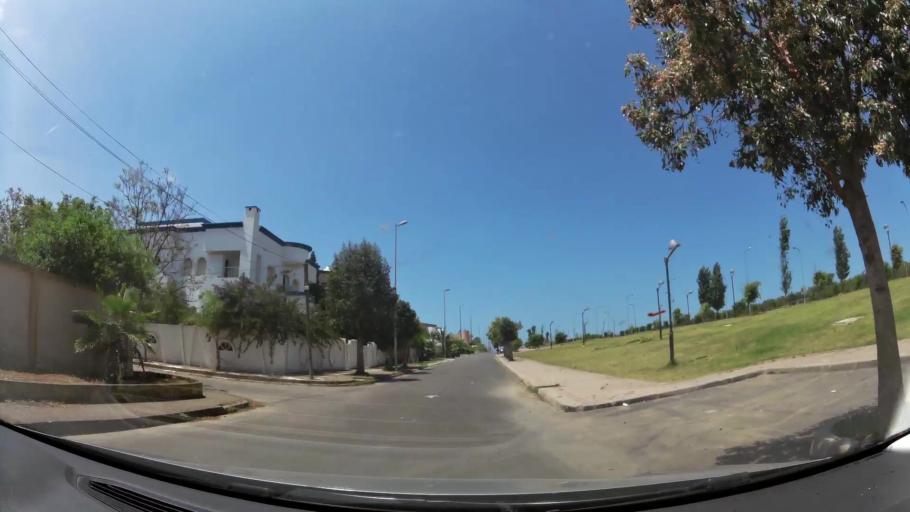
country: MA
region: Gharb-Chrarda-Beni Hssen
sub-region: Kenitra Province
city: Kenitra
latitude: 34.2738
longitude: -6.6155
